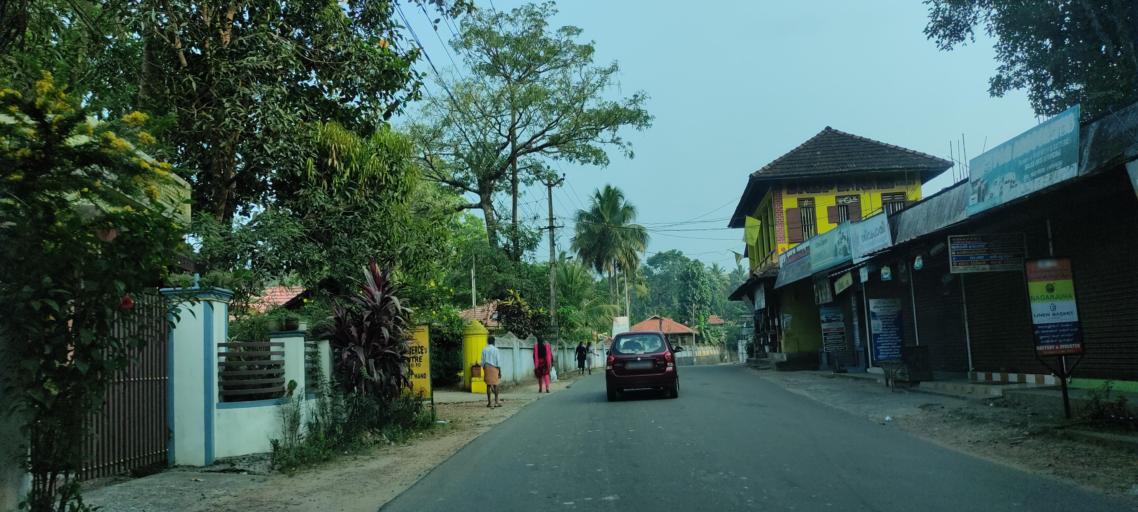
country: IN
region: Kerala
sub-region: Kottayam
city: Vaikam
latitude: 9.7090
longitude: 76.4766
